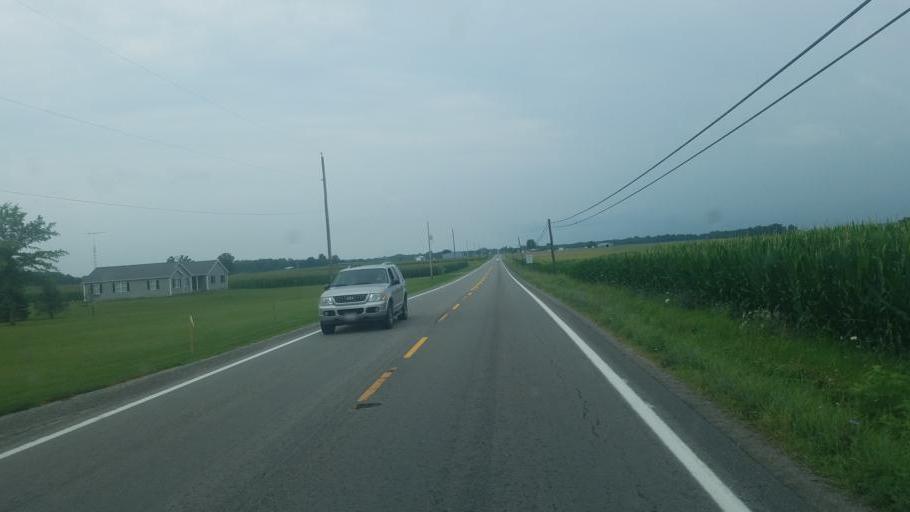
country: US
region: Ohio
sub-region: Hardin County
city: Kenton
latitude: 40.6361
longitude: -83.6218
